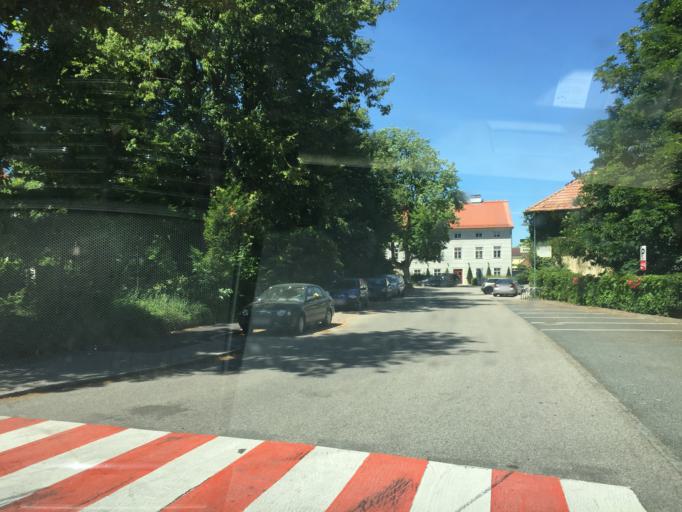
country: AT
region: Lower Austria
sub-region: Politischer Bezirk Sankt Polten
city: Herzogenburg
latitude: 48.2392
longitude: 15.6981
